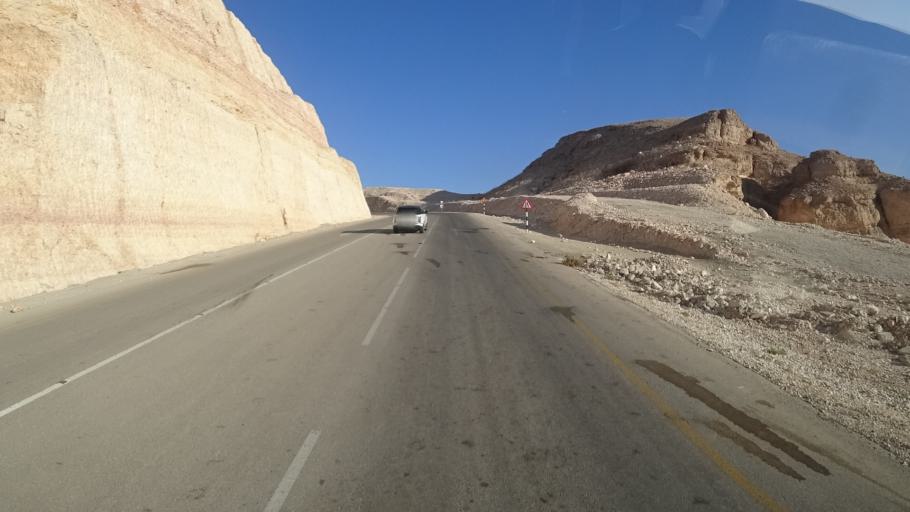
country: YE
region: Al Mahrah
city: Hawf
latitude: 17.0929
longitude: 53.0613
